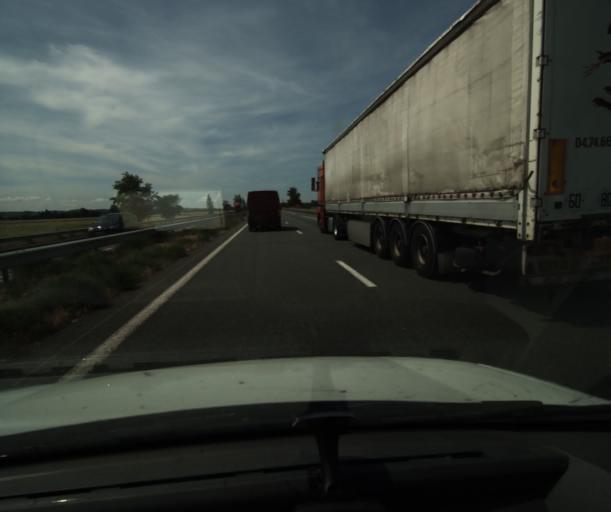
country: FR
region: Languedoc-Roussillon
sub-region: Departement de l'Aude
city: Saint-Martin-Lalande
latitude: 43.2610
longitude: 2.0236
